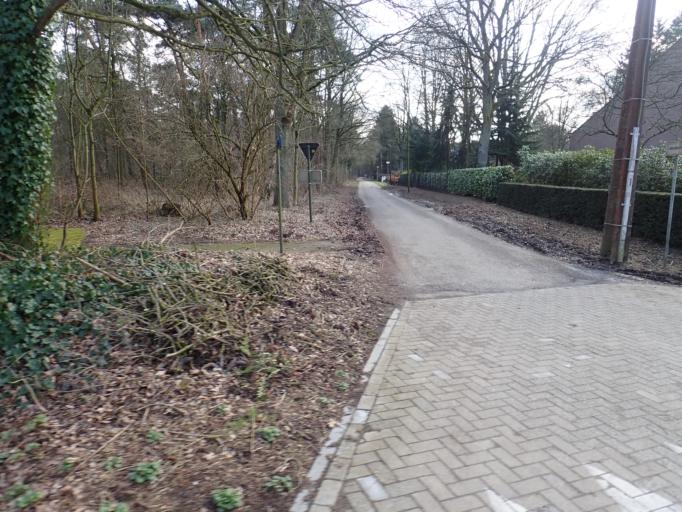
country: BE
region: Flanders
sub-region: Provincie Antwerpen
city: Zandhoven
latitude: 51.1944
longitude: 4.6941
